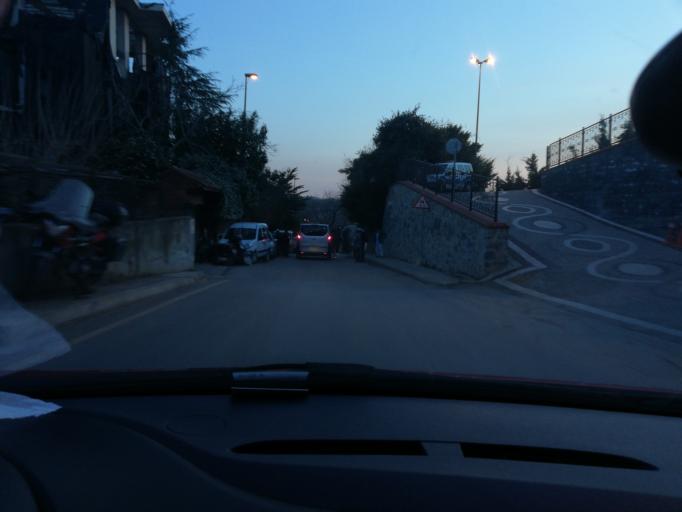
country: TR
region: Istanbul
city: UEskuedar
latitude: 41.0534
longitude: 29.0574
